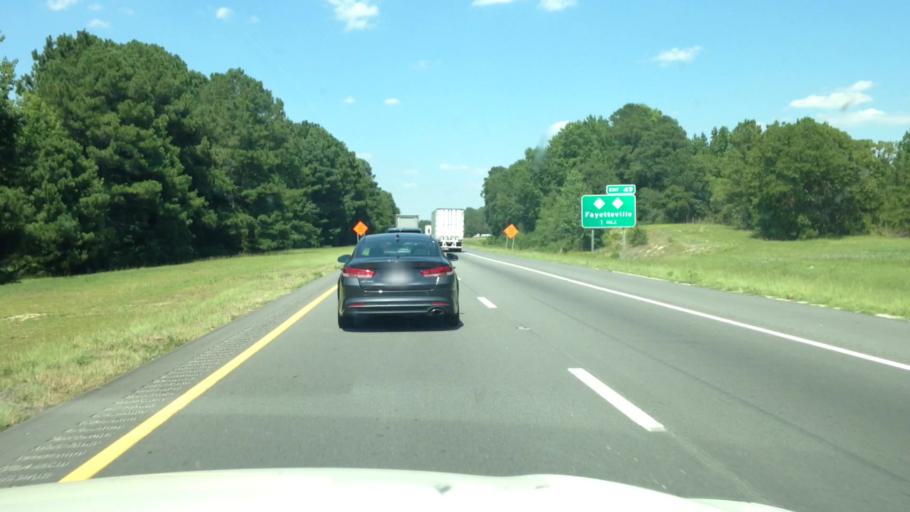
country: US
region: North Carolina
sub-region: Cumberland County
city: Vander
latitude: 34.9915
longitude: -78.8357
